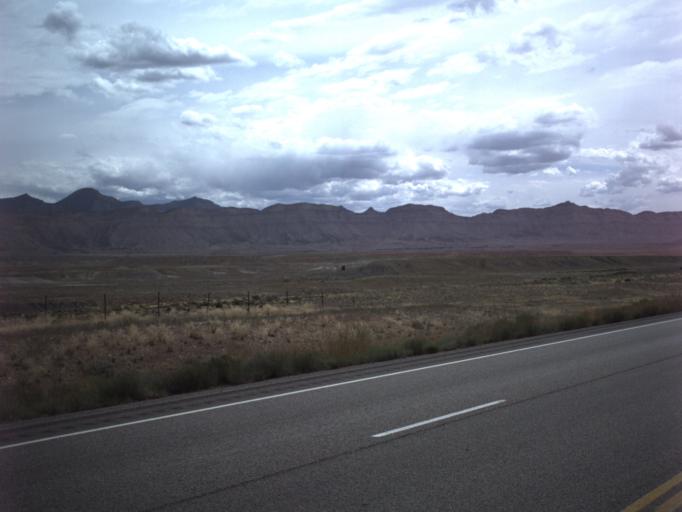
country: US
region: Utah
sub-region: Carbon County
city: East Carbon City
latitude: 39.3876
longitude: -110.4121
